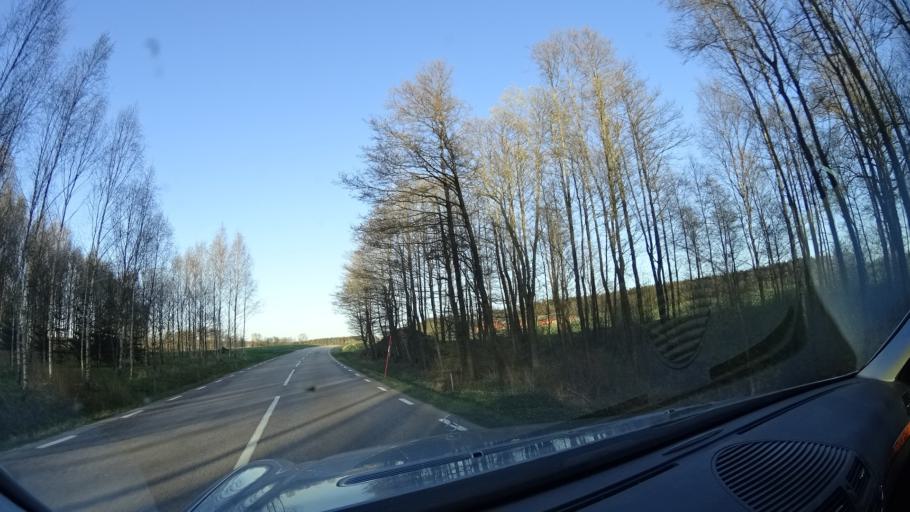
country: SE
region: Skane
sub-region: Svalovs Kommun
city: Kagerod
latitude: 55.9786
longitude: 13.1646
